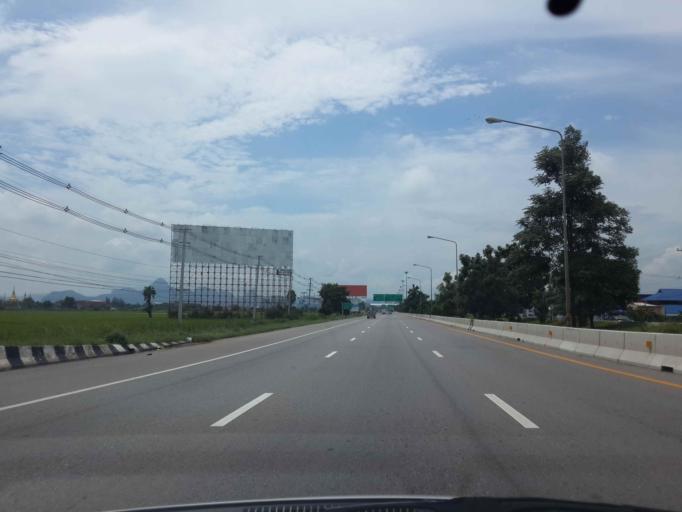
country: TH
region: Ratchaburi
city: Pak Tho
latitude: 13.3412
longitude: 99.8450
